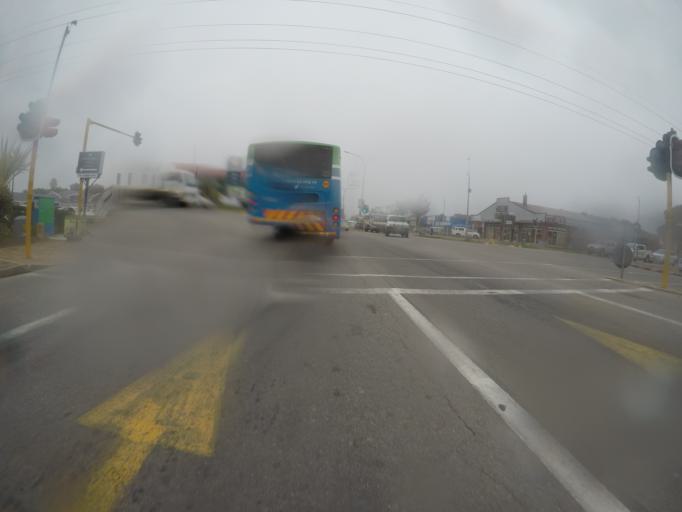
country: ZA
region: Western Cape
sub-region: Eden District Municipality
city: George
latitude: -33.9720
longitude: 22.4463
